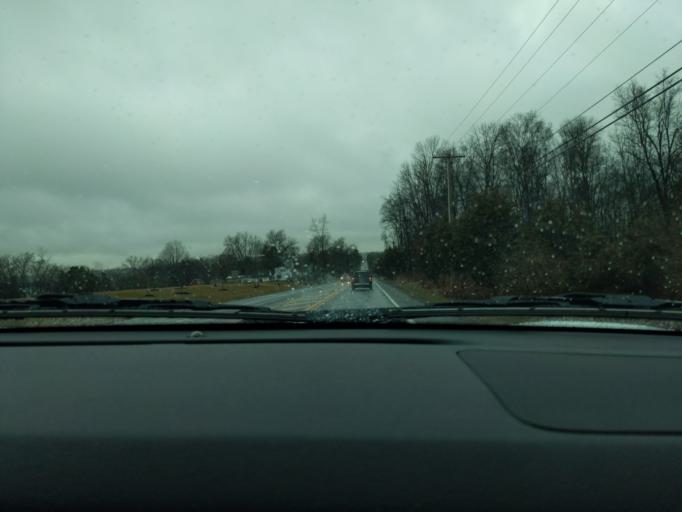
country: US
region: Pennsylvania
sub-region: Bucks County
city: Dublin
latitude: 40.3860
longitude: -75.2255
